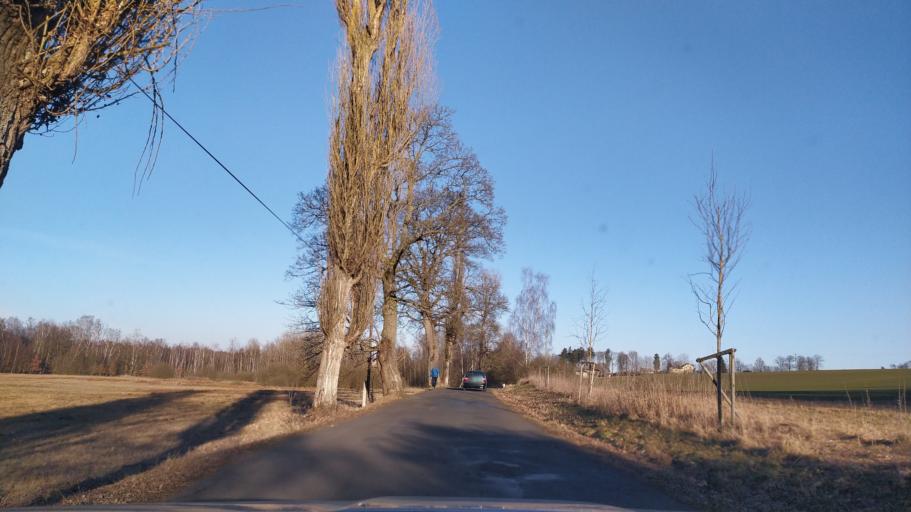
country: CZ
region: Karlovarsky
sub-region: Okres Cheb
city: Frantiskovy Lazne
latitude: 50.1119
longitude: 12.3456
